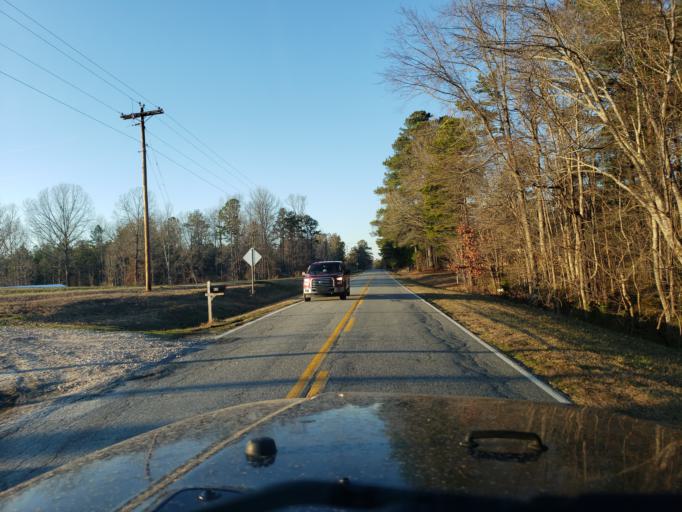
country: US
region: South Carolina
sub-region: Cherokee County
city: Blacksburg
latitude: 35.0536
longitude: -81.4242
